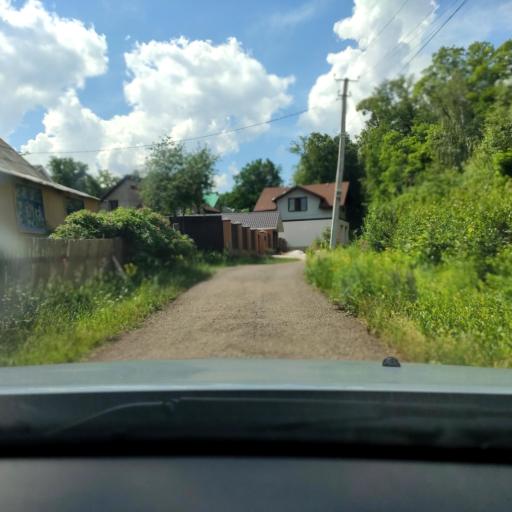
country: RU
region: Bashkortostan
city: Avdon
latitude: 54.7095
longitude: 55.7326
